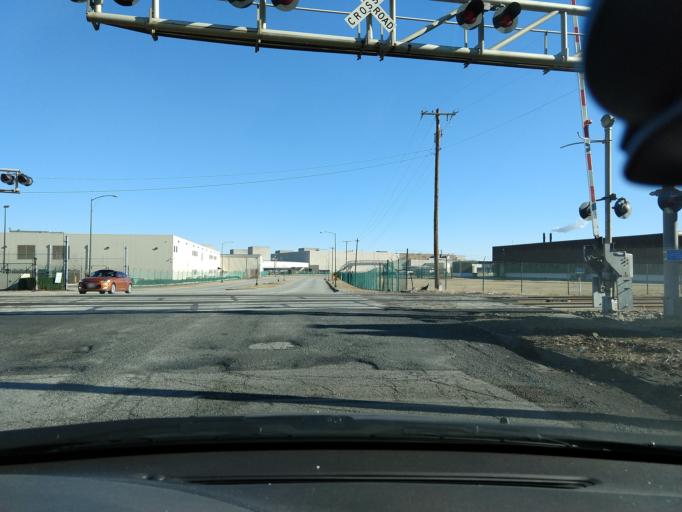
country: US
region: Virginia
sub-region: Chesterfield County
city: Bensley
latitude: 37.4726
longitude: -77.4388
